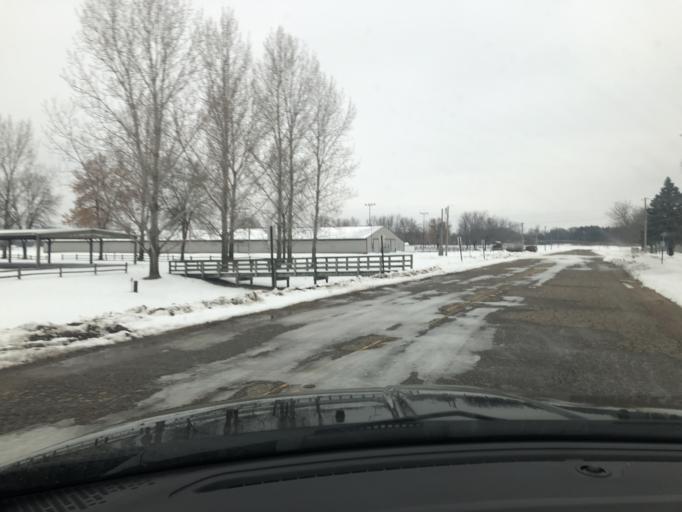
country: US
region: Minnesota
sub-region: Washington County
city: Lake Elmo
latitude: 45.0097
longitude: -92.8582
